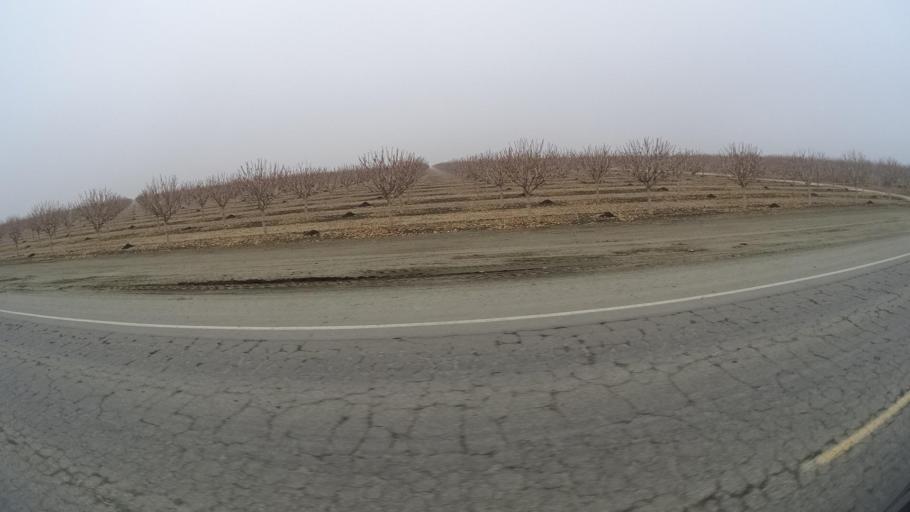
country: US
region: California
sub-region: Kern County
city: Buttonwillow
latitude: 35.4302
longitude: -119.5184
